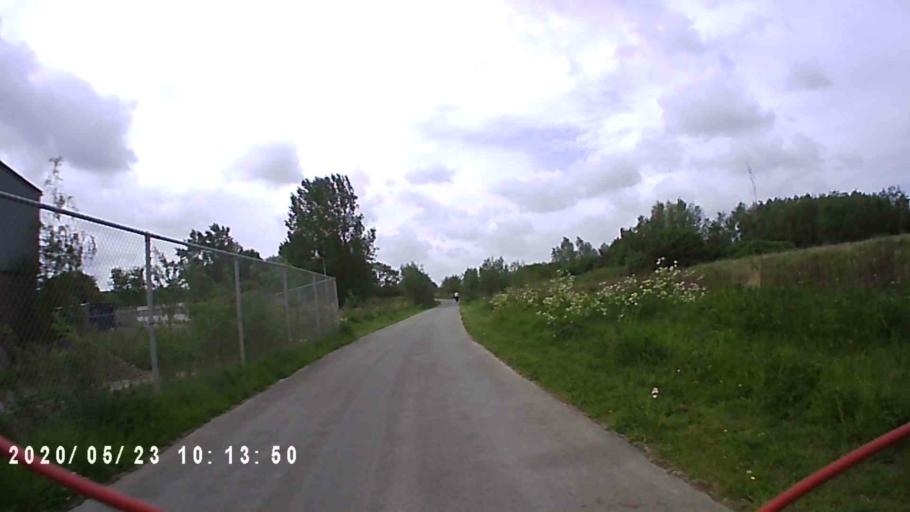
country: NL
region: Groningen
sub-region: Gemeente Appingedam
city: Appingedam
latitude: 53.3139
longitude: 6.8556
